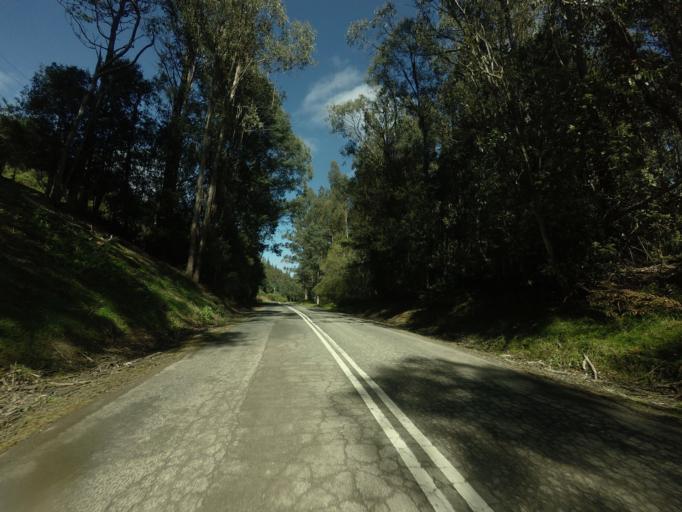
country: AU
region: Tasmania
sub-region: Derwent Valley
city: New Norfolk
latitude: -42.7598
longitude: 146.6124
